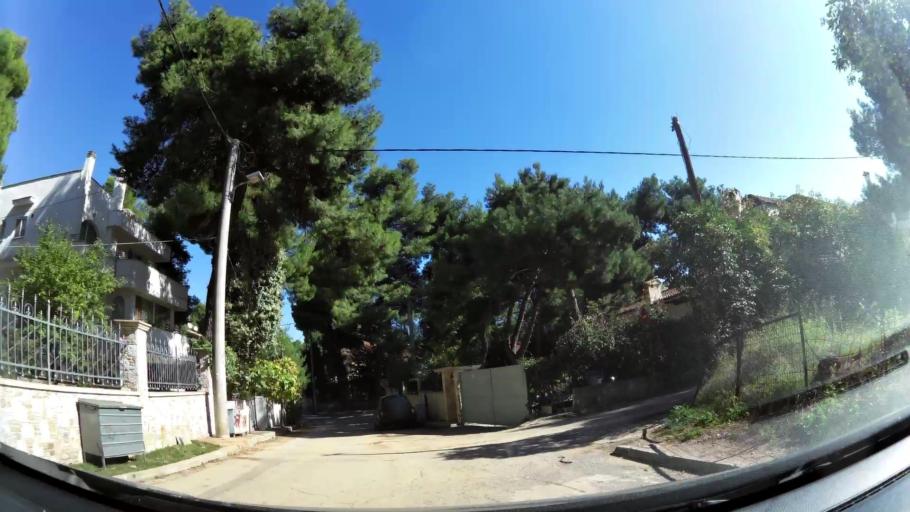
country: GR
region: Attica
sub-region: Nomarchia Anatolikis Attikis
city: Drosia
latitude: 38.1176
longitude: 23.8593
